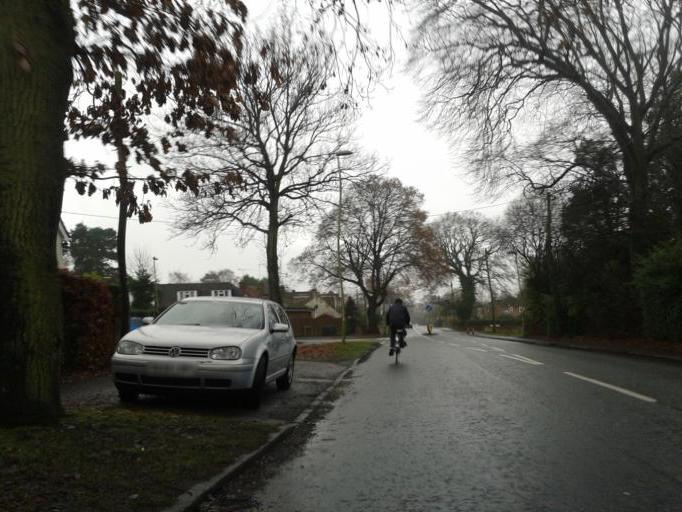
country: GB
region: England
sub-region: Hampshire
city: Farnborough
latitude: 51.3007
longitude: -0.7607
